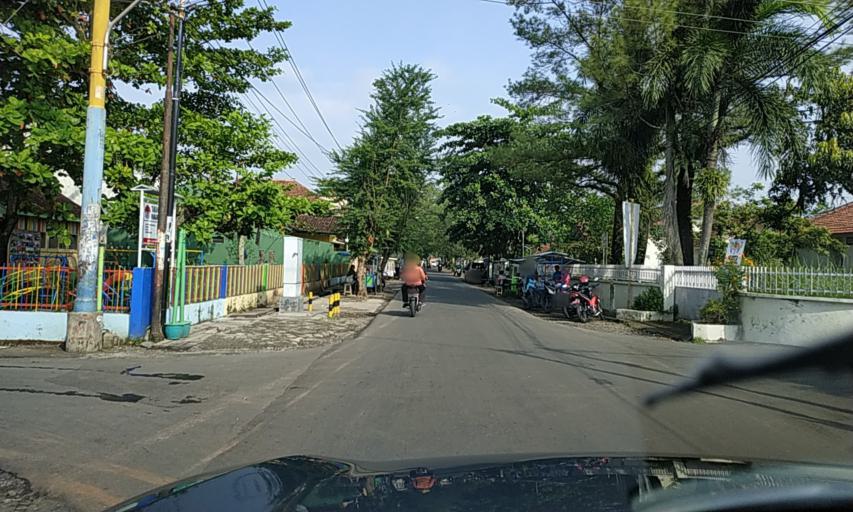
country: ID
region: Central Java
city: Purwokerto
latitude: -7.4238
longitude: 109.2406
